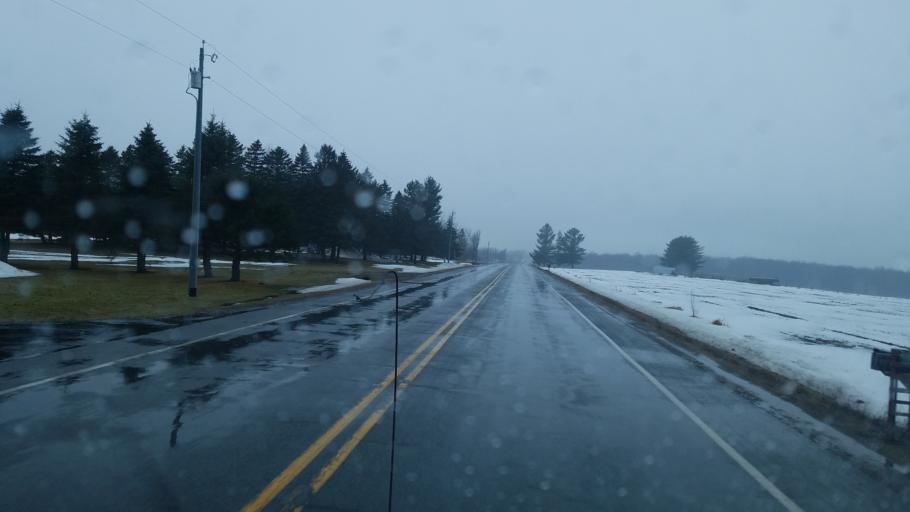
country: US
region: Wisconsin
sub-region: Marathon County
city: Spencer
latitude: 44.6777
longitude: -90.2703
